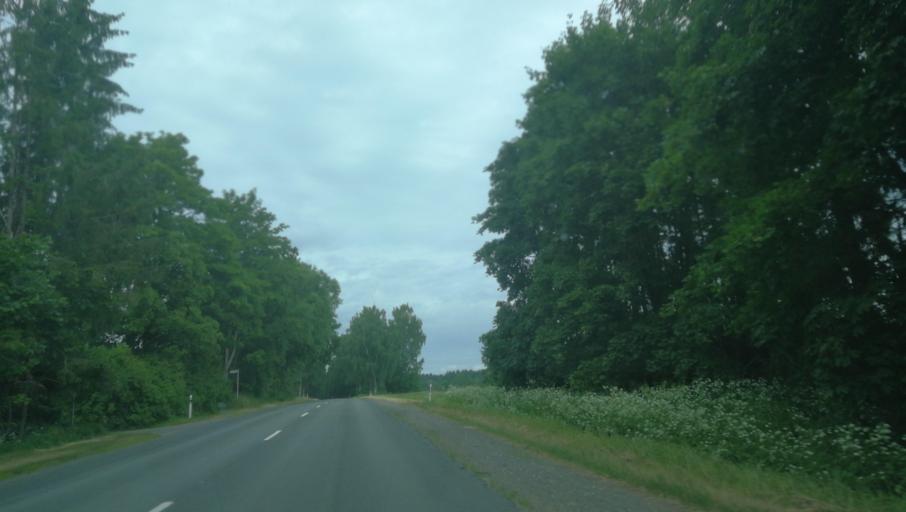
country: LV
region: Valmieras Rajons
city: Valmiera
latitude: 57.6690
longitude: 25.4299
